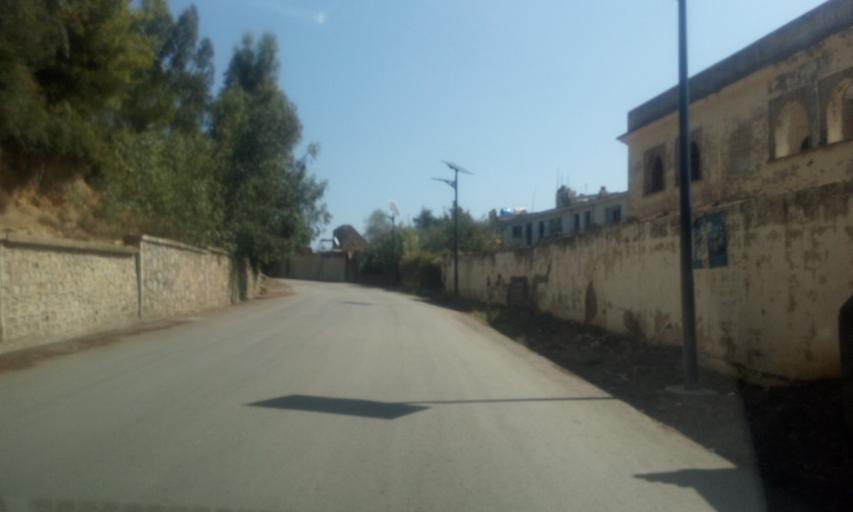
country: DZ
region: Bejaia
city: Bejaia
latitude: 36.7604
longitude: 5.0832
